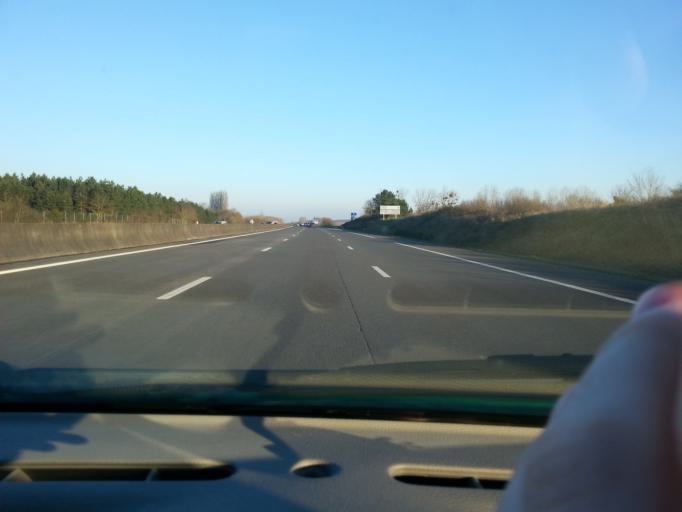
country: FR
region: Pays de la Loire
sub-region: Departement de la Sarthe
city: Champagne
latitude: 48.0507
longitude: 0.3063
